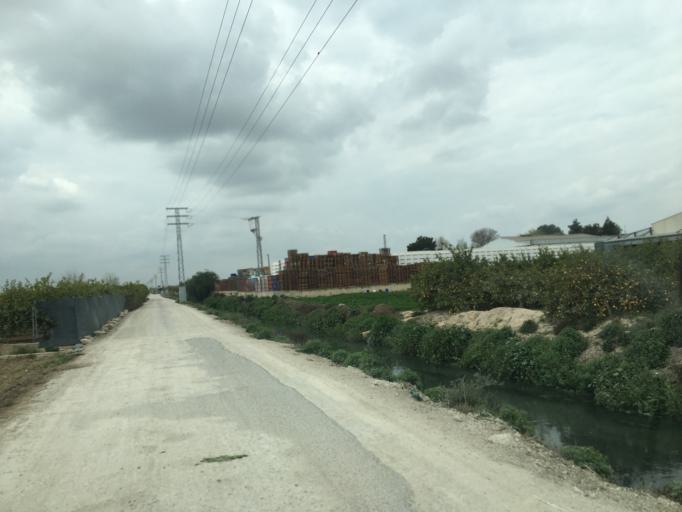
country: ES
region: Murcia
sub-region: Murcia
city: Santomera
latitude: 38.0457
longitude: -1.0334
